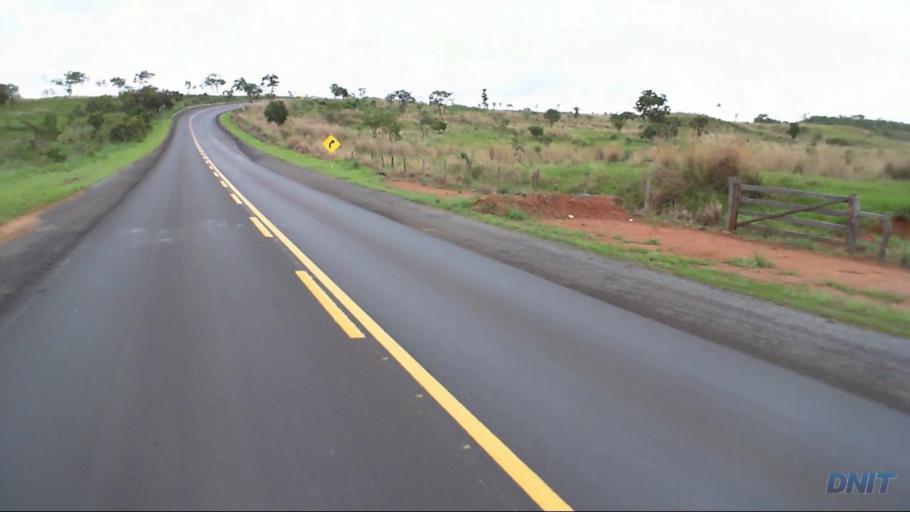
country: BR
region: Goias
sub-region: Padre Bernardo
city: Padre Bernardo
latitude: -15.2101
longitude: -48.4730
